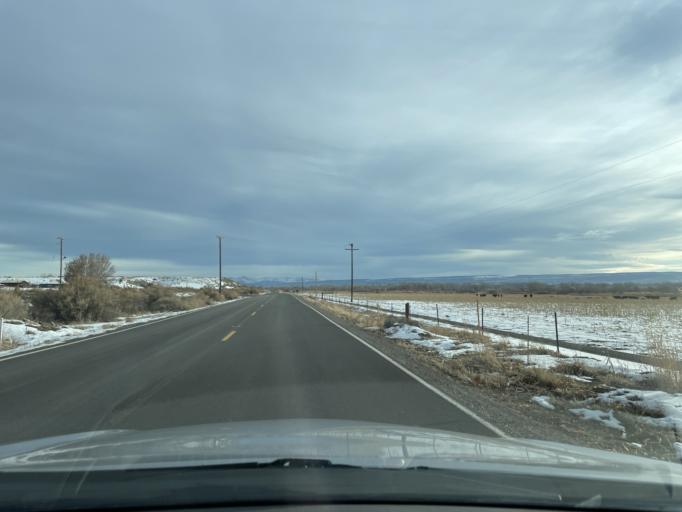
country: US
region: Colorado
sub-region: Montrose County
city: Olathe
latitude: 38.6577
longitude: -107.9975
